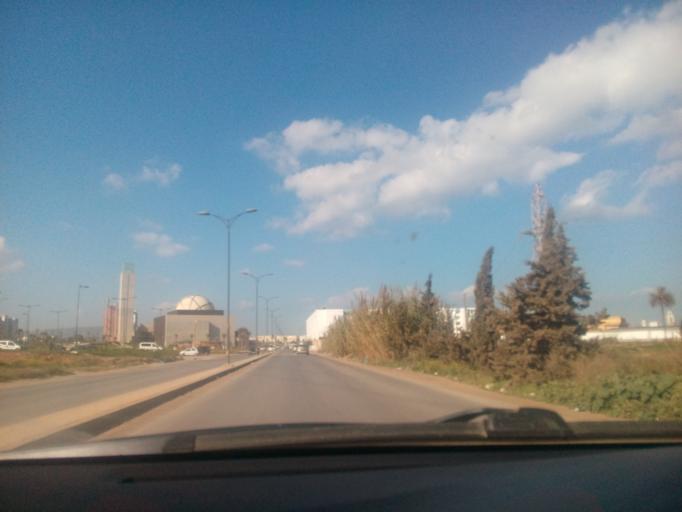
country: DZ
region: Oran
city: Es Senia
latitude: 35.6777
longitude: -0.5981
